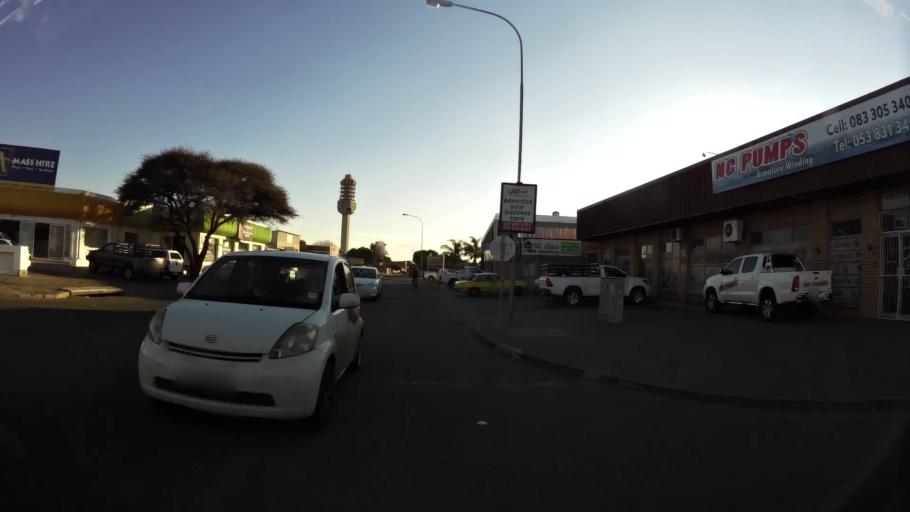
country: ZA
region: Northern Cape
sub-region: Frances Baard District Municipality
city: Kimberley
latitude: -28.7431
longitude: 24.7547
